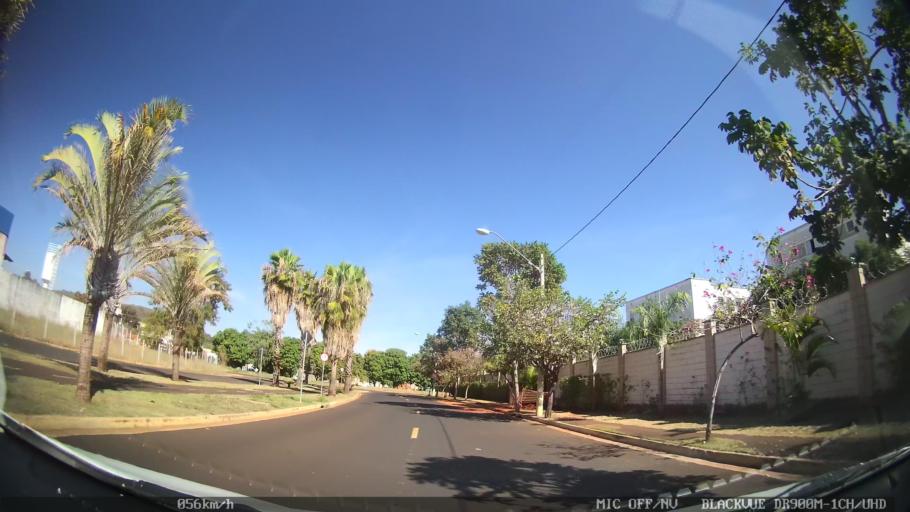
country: BR
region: Sao Paulo
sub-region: Ribeirao Preto
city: Ribeirao Preto
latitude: -21.2222
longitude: -47.7626
